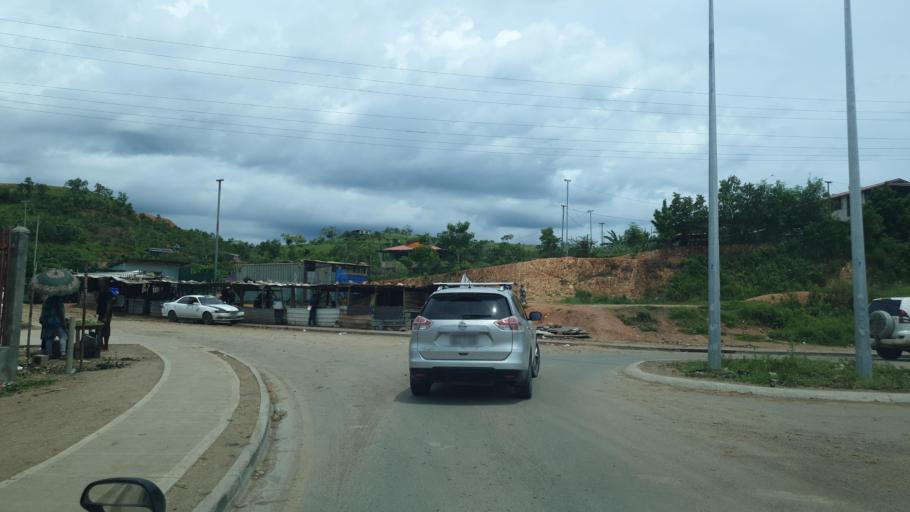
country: PG
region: National Capital
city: Port Moresby
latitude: -9.5101
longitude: 147.2420
